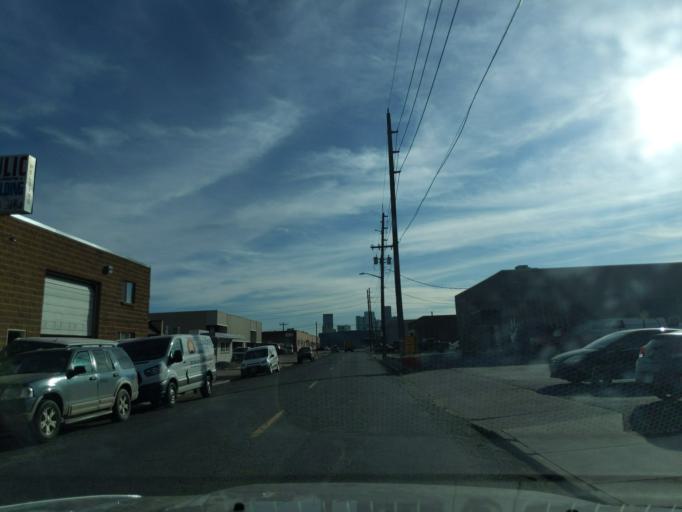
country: US
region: Colorado
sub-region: Denver County
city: Denver
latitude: 39.7764
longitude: -104.9876
